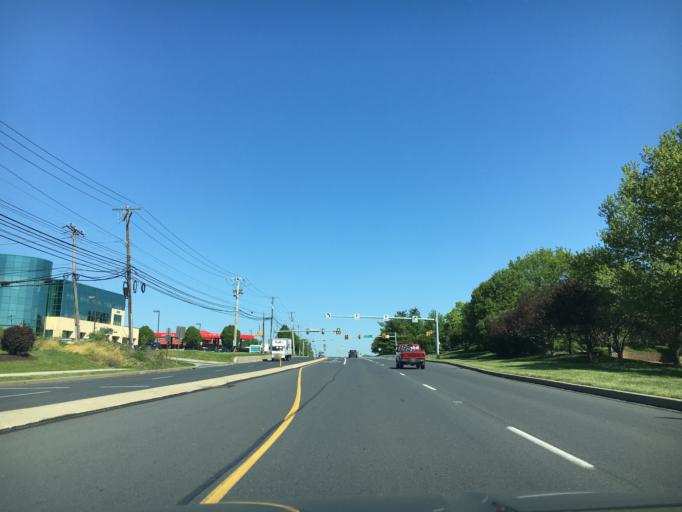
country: US
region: Pennsylvania
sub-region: Northampton County
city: Bethlehem
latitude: 40.6545
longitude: -75.4152
